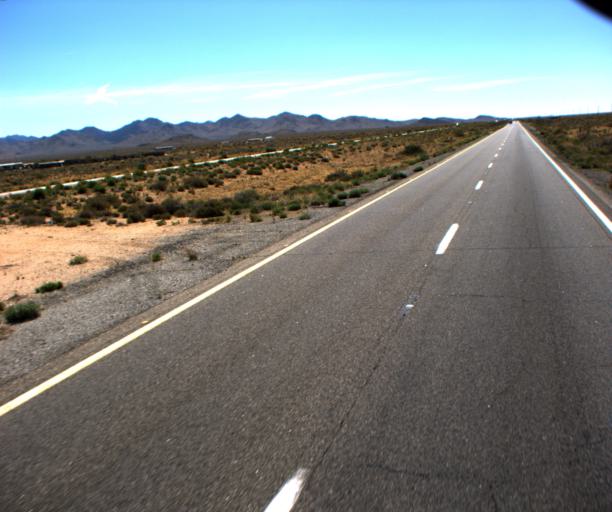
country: US
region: Arizona
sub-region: Mohave County
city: Dolan Springs
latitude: 35.5004
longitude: -114.3325
